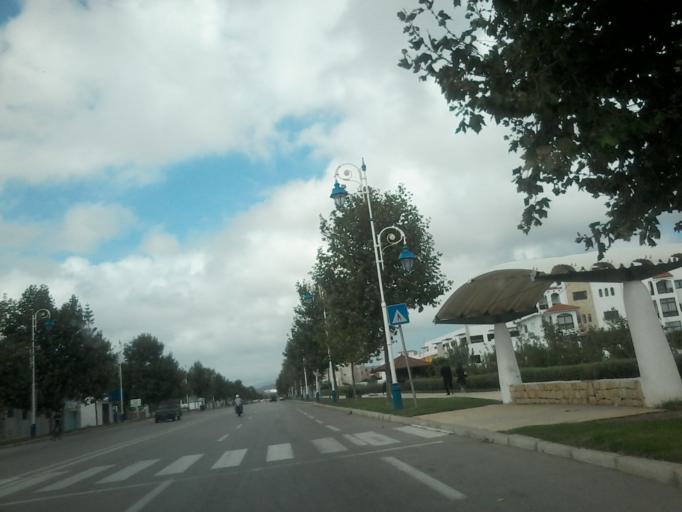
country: MA
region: Tanger-Tetouan
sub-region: Tetouan
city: Martil
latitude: 35.6317
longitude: -5.2850
